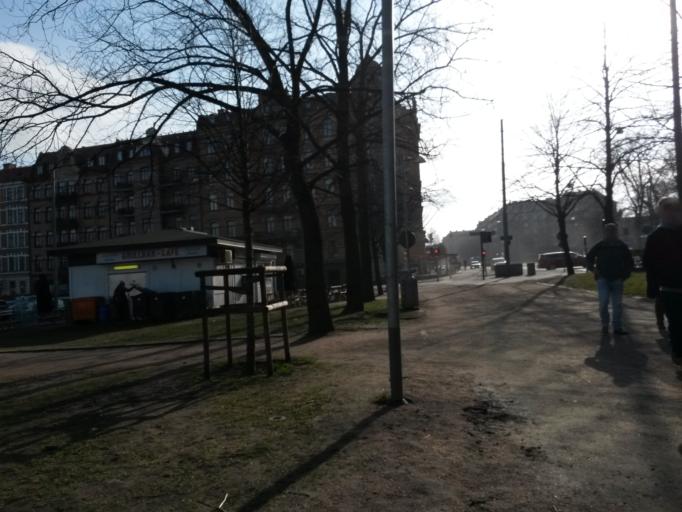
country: SE
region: Vaestra Goetaland
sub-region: Goteborg
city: Goeteborg
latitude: 57.7001
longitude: 11.9791
